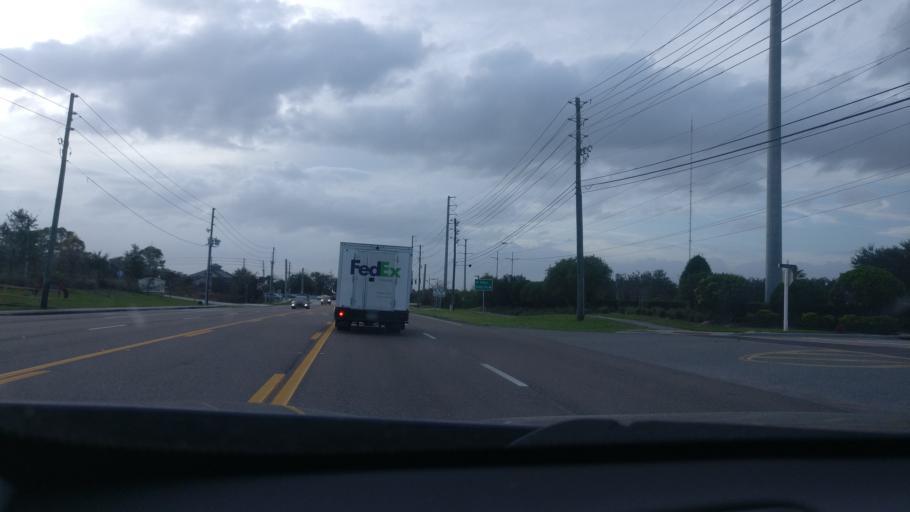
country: US
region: Florida
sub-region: Volusia County
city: DeBary
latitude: 28.9120
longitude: -81.3005
